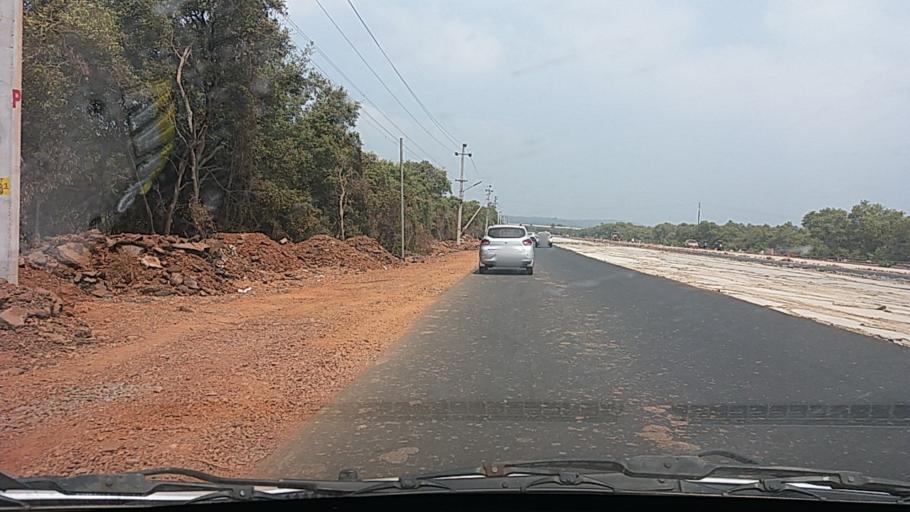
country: IN
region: Goa
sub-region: North Goa
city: Taleigao
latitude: 15.4841
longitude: 73.8468
